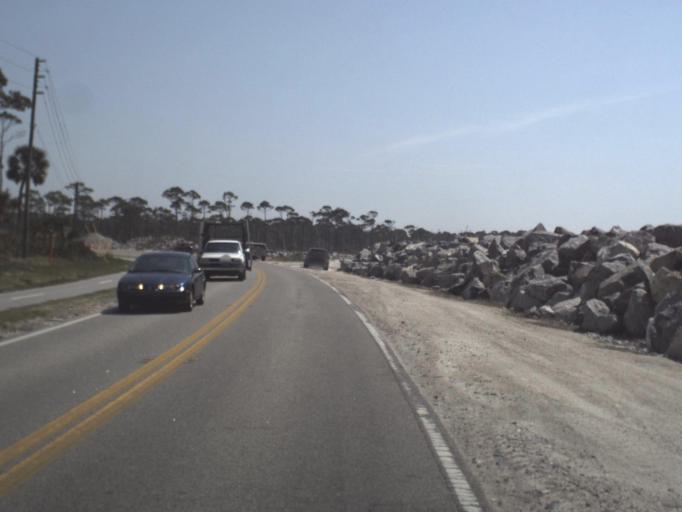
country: US
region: Florida
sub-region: Gulf County
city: Port Saint Joe
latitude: 29.6774
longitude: -85.3644
